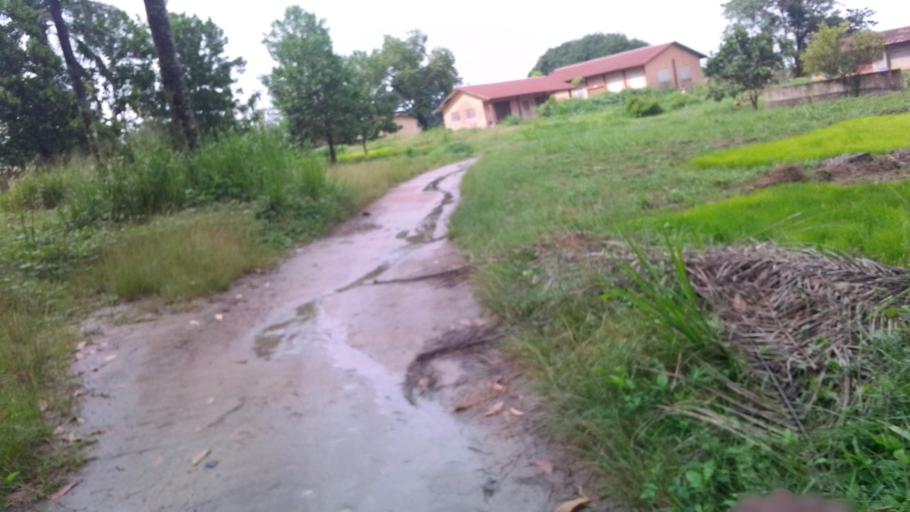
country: SL
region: Eastern Province
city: Kenema
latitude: 7.8536
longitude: -11.2029
